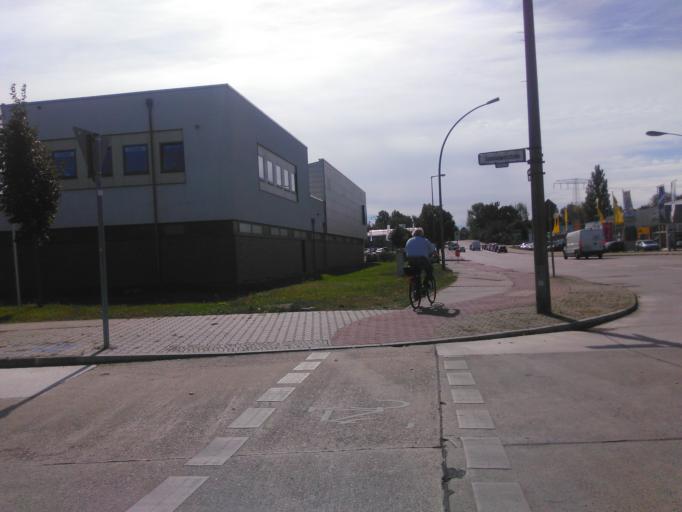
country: DE
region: Berlin
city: Altglienicke
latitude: 52.4246
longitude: 13.5266
